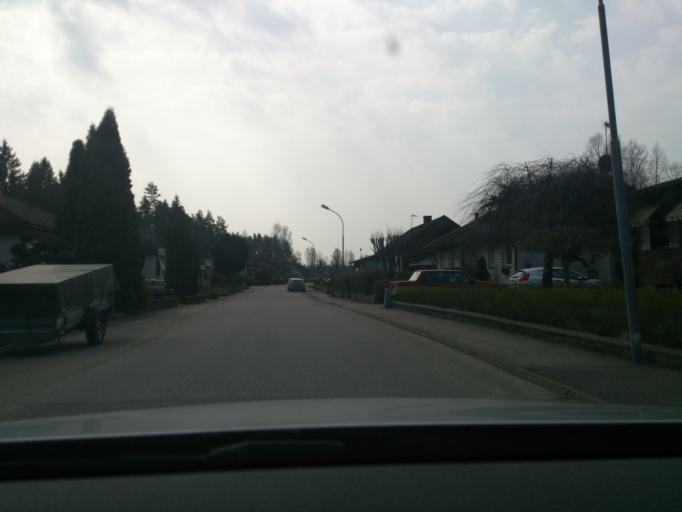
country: SE
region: Kronoberg
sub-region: Alvesta Kommun
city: Moheda
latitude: 57.0004
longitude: 14.5843
